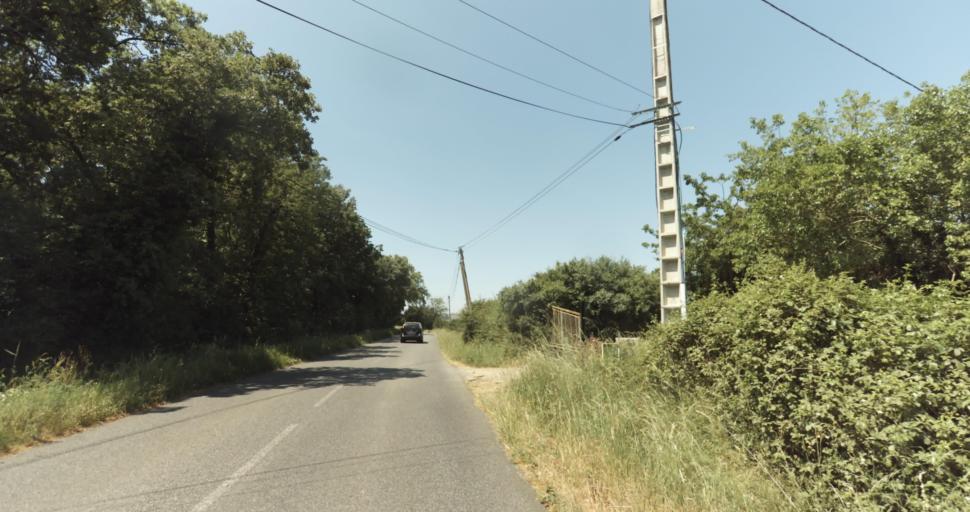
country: FR
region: Midi-Pyrenees
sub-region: Departement de la Haute-Garonne
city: La Salvetat-Saint-Gilles
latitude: 43.5984
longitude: 1.2704
